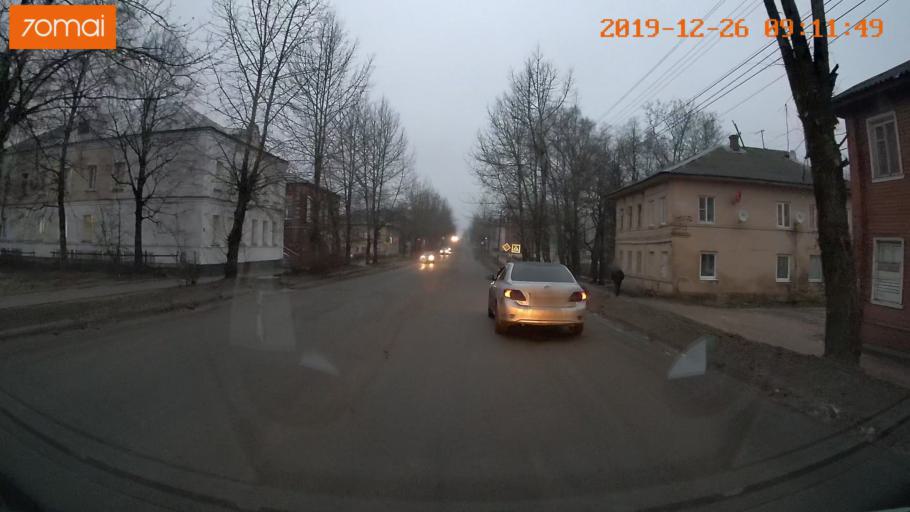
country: RU
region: Vologda
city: Gryazovets
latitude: 58.8778
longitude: 40.2529
